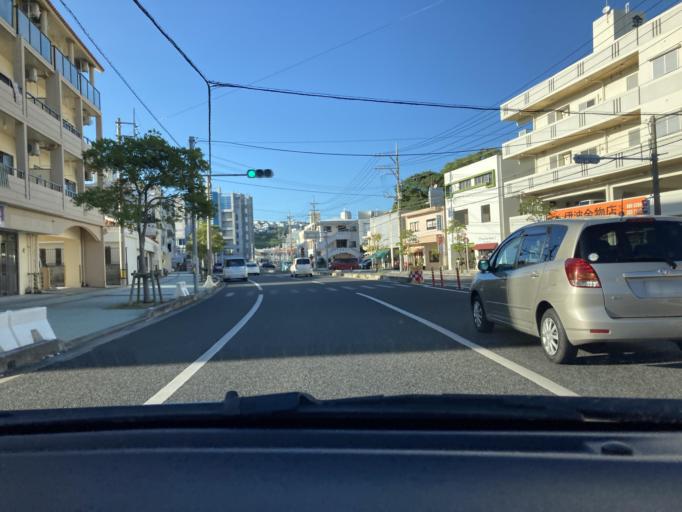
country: JP
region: Okinawa
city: Tomigusuku
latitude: 26.1937
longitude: 127.7279
